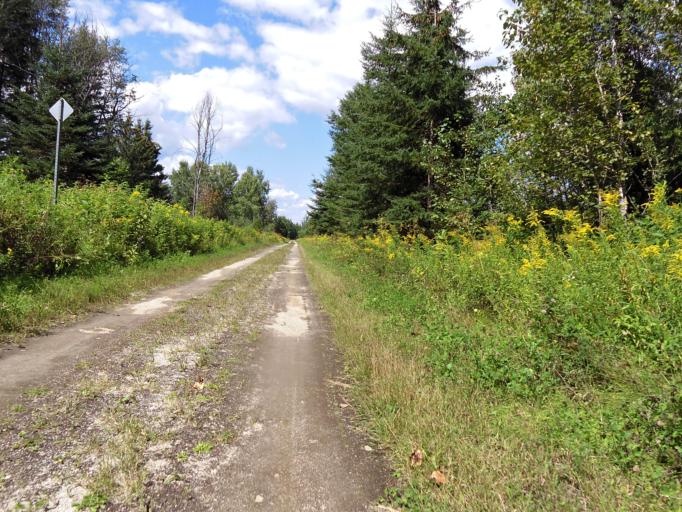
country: CA
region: Quebec
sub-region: Outaouais
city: Wakefield
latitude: 45.8700
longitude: -76.0247
